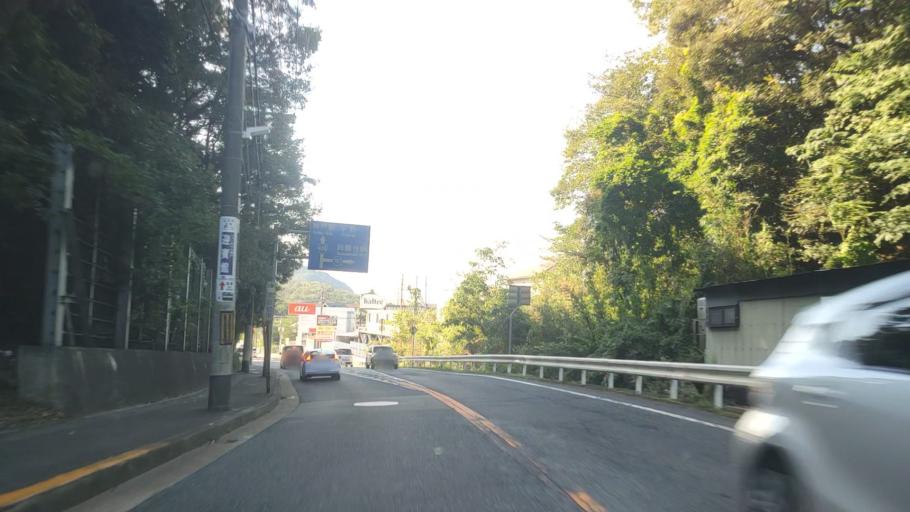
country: JP
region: Hyogo
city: Kobe
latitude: 34.7317
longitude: 135.1592
